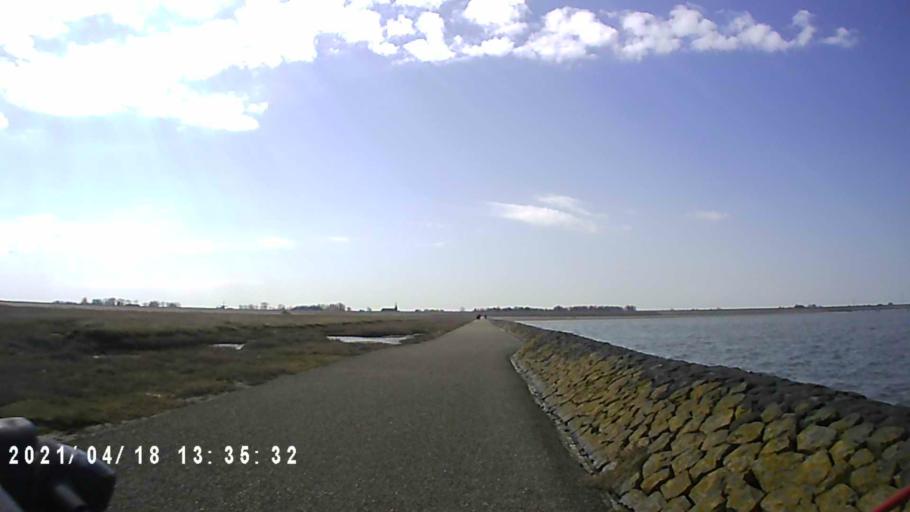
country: NL
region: Friesland
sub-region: Gemeente Dongeradeel
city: Anjum
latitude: 53.4085
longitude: 6.0905
